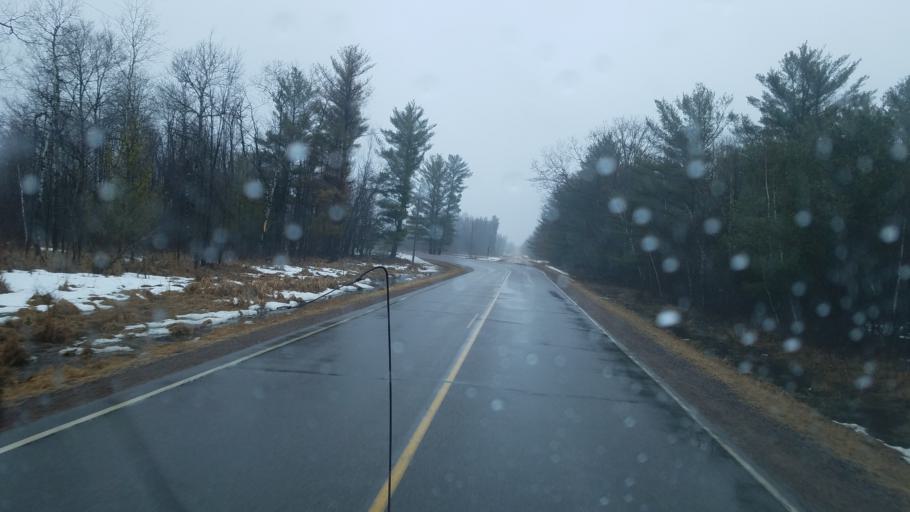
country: US
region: Wisconsin
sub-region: Wood County
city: Marshfield
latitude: 44.5103
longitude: -90.2792
